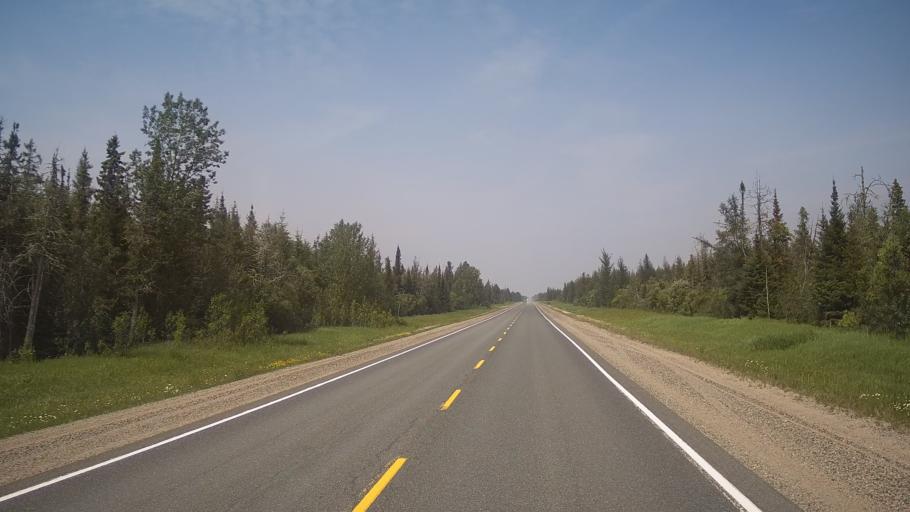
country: CA
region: Ontario
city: Timmins
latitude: 48.7866
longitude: -81.3652
